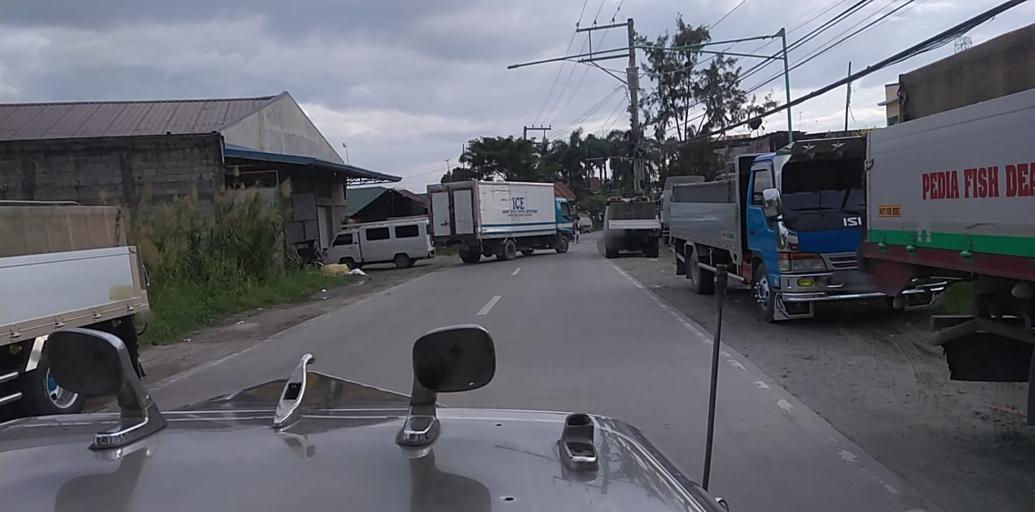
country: PH
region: Central Luzon
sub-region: Province of Pampanga
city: Minalin
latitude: 14.9886
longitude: 120.7045
